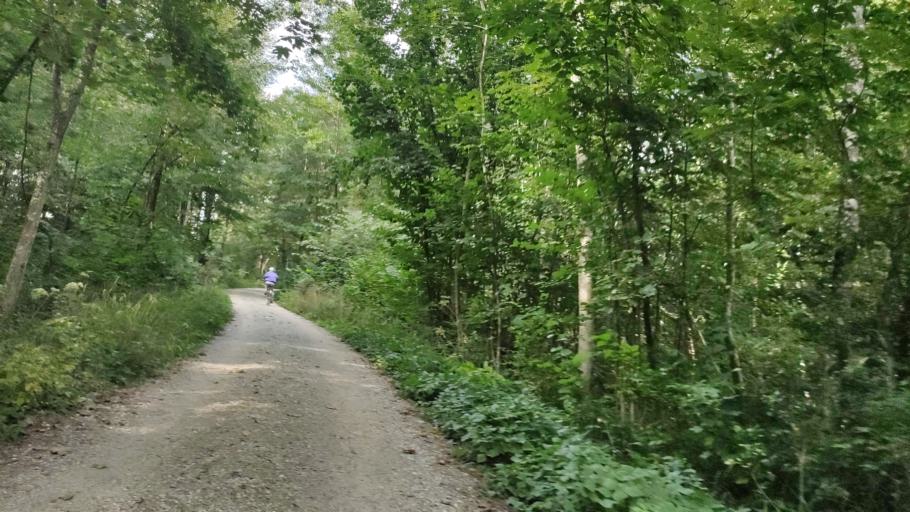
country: DE
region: Bavaria
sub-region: Swabia
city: Klosterlechfeld
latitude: 48.1379
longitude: 10.8647
